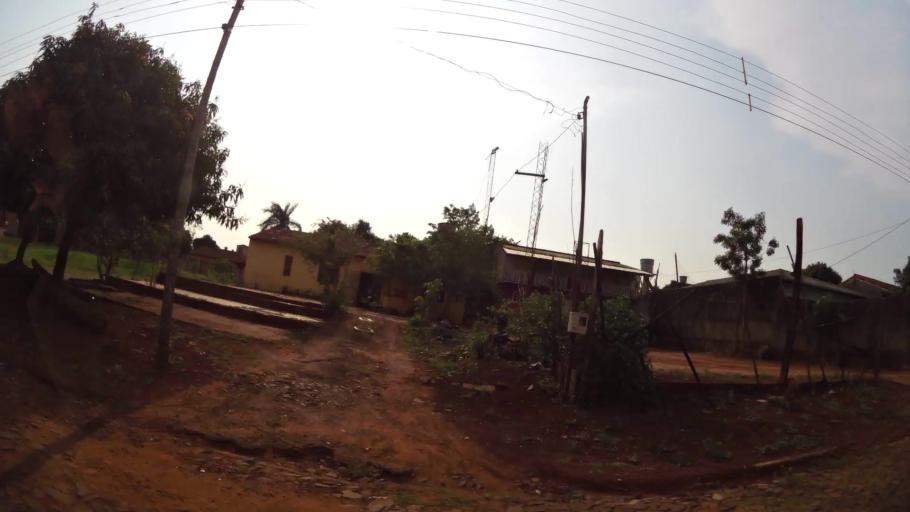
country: PY
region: Alto Parana
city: Ciudad del Este
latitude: -25.4866
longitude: -54.6527
